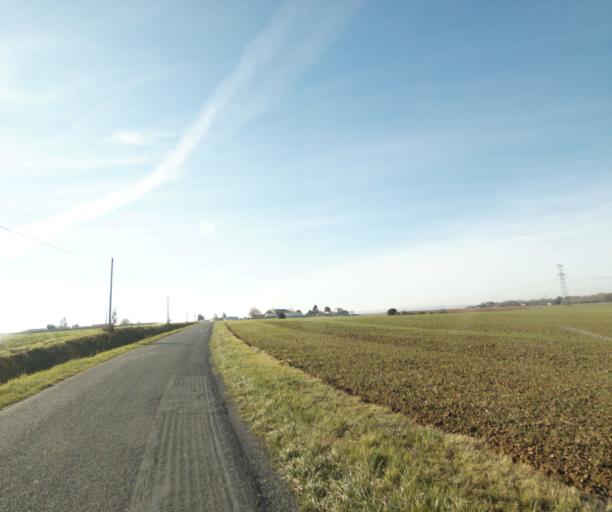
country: FR
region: Poitou-Charentes
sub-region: Departement de la Charente-Maritime
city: Chaniers
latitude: 45.7397
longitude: -0.5742
